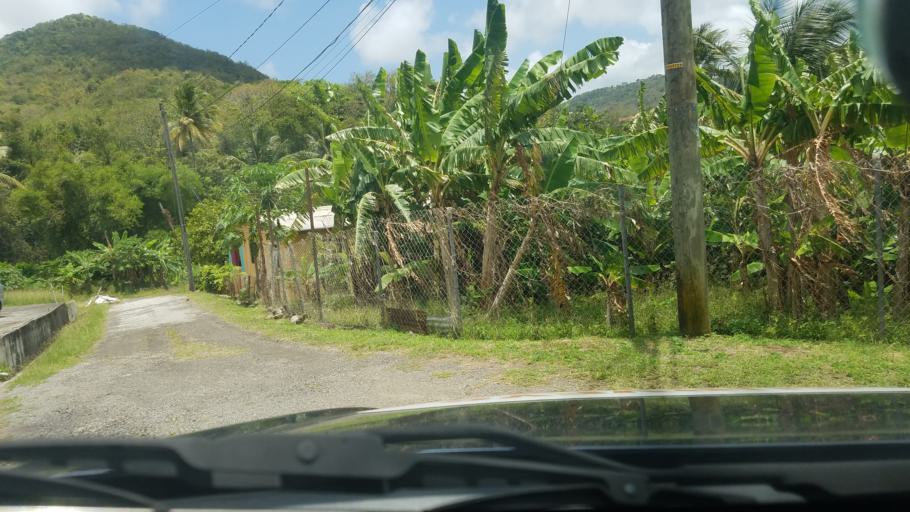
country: LC
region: Gros-Islet
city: Gros Islet
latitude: 14.0559
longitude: -60.9296
